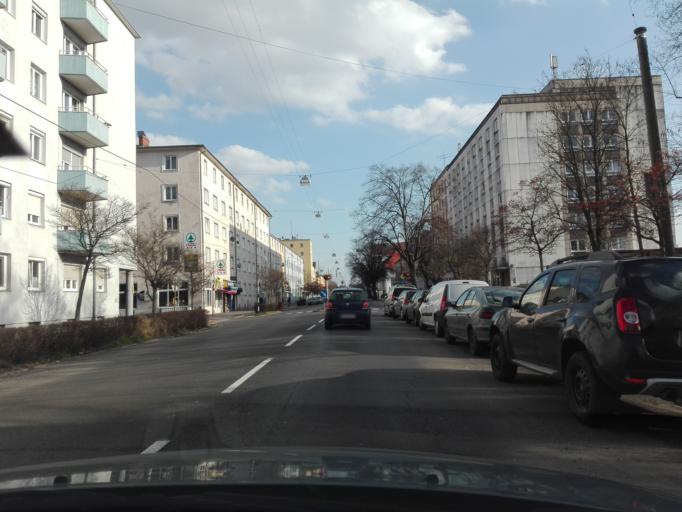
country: AT
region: Upper Austria
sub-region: Linz Stadt
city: Linz
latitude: 48.2955
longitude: 14.3093
